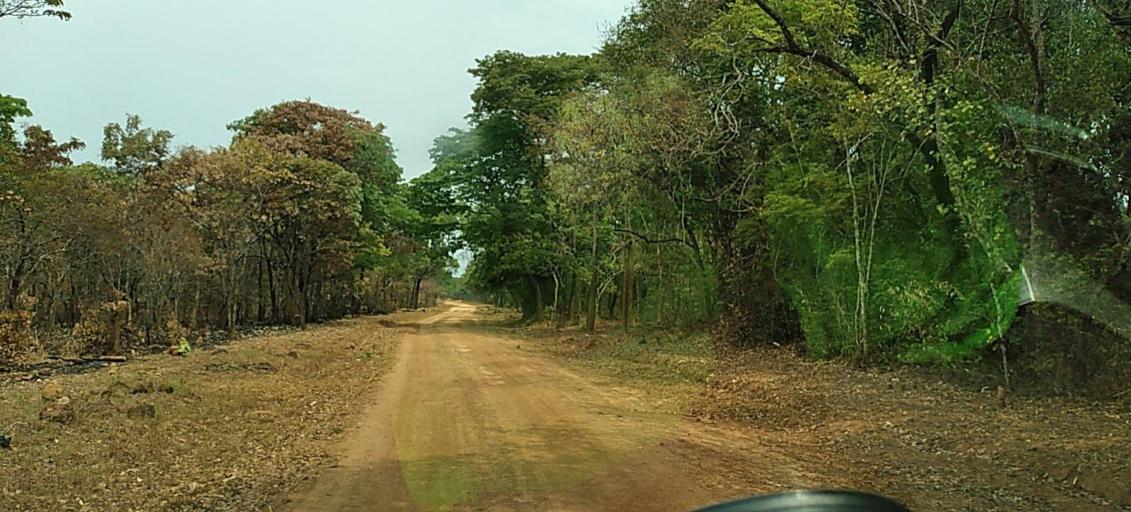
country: ZM
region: North-Western
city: Solwezi
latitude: -12.9555
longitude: 26.5647
